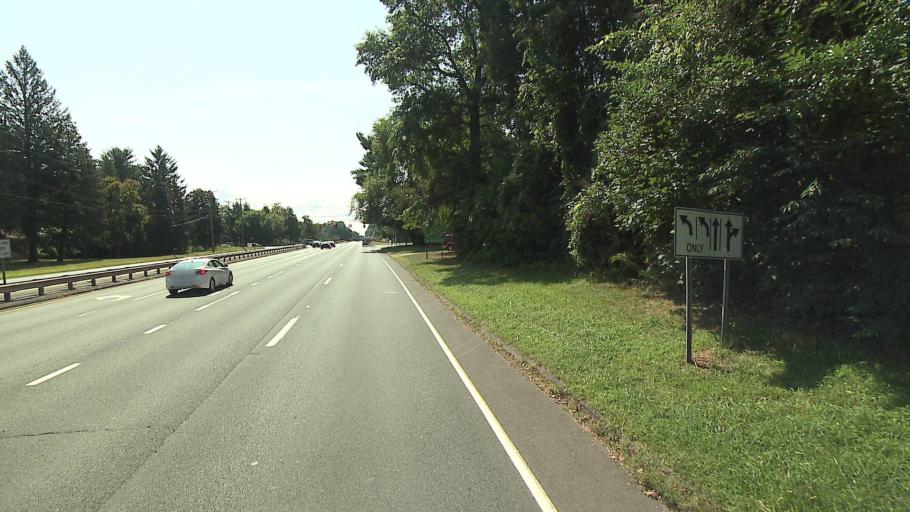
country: US
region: Connecticut
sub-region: Hartford County
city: South Windsor
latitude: 41.8590
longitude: -72.6027
